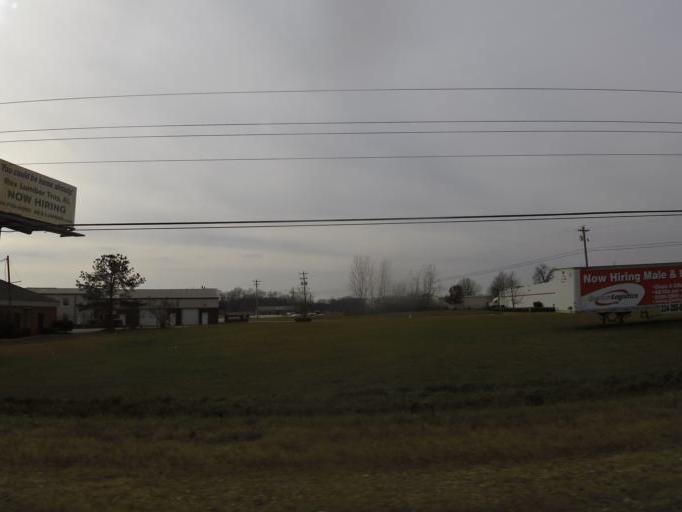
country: US
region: Alabama
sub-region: Montgomery County
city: Pike Road
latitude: 32.3018
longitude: -86.2061
